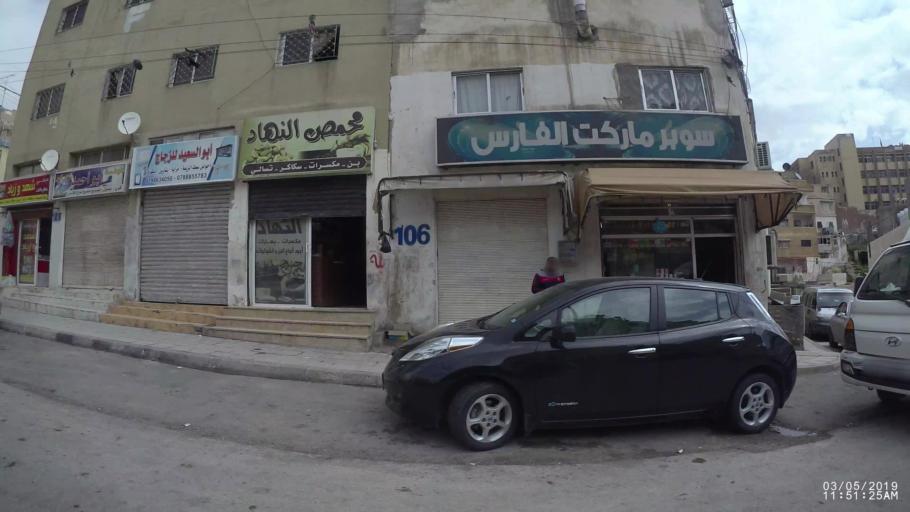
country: JO
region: Amman
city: Amman
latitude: 31.9592
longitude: 35.9345
